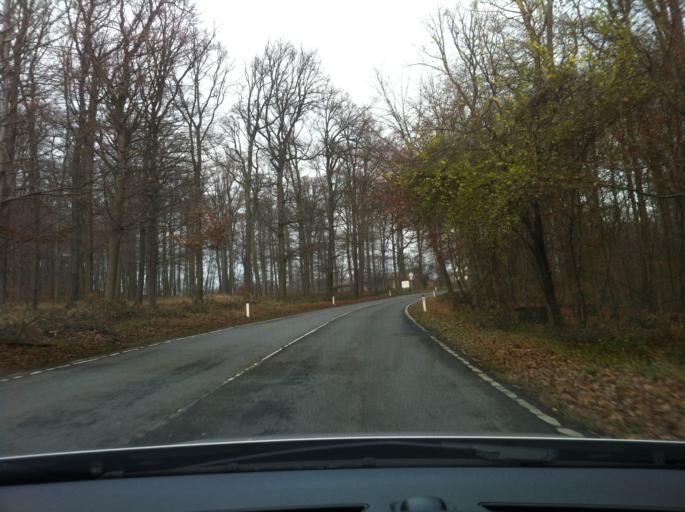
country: AT
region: Lower Austria
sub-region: Politischer Bezirk Wien-Umgebung
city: Purkersdorf
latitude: 48.2289
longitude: 16.2558
